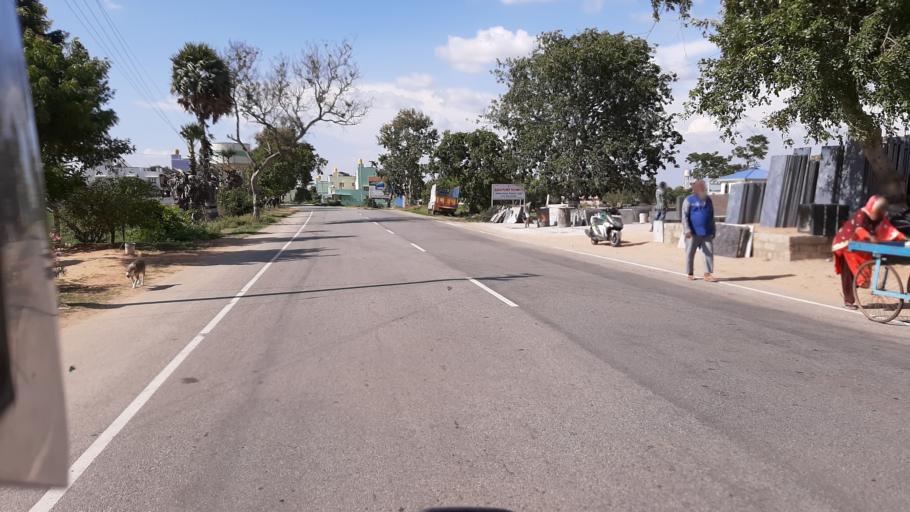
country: IN
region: Tamil Nadu
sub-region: Krishnagiri
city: Denkanikota
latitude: 12.5547
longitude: 77.7853
